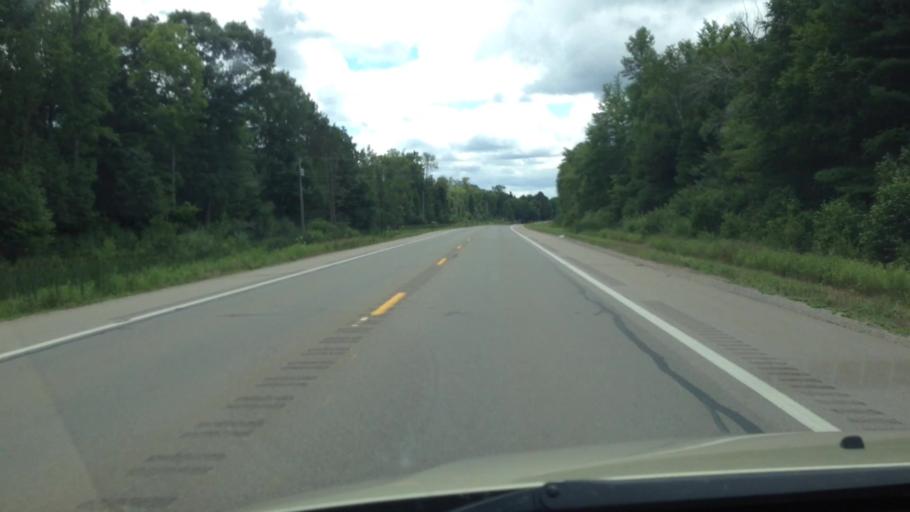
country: US
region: Michigan
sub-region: Menominee County
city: Menominee
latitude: 45.2243
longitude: -87.5138
